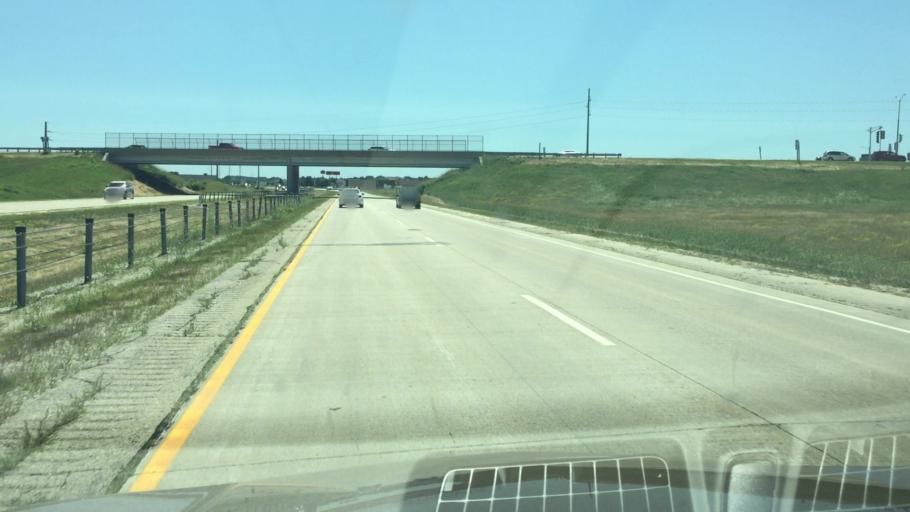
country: US
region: Wisconsin
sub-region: Dodge County
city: Beaver Dam
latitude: 43.4885
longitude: -88.8145
